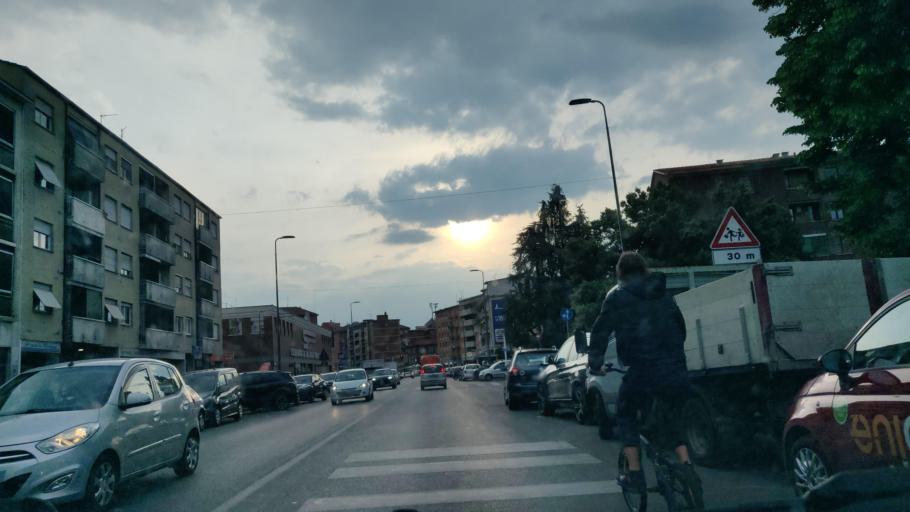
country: IT
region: Lombardy
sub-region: Citta metropolitana di Milano
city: Cesano Boscone
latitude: 45.4604
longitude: 9.1121
